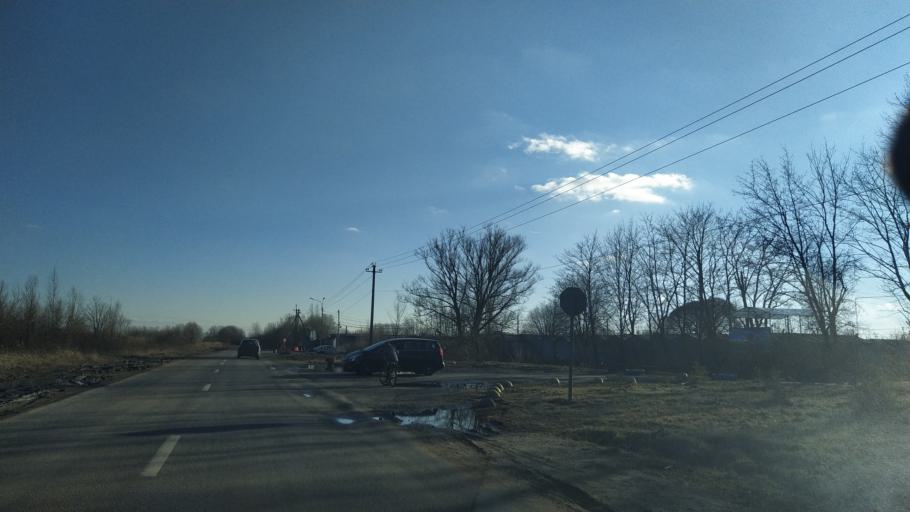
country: RU
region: St.-Petersburg
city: Pushkin
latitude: 59.6943
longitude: 30.3960
